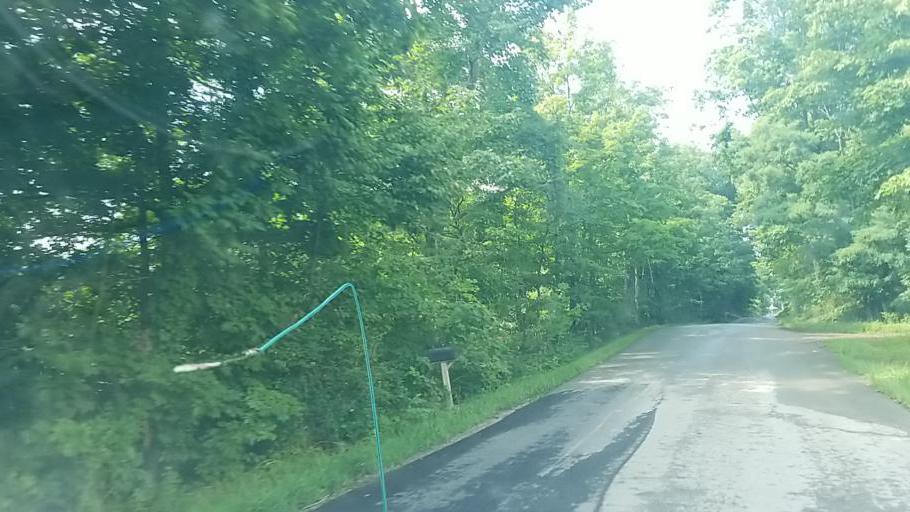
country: US
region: Ohio
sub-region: Medina County
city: Lodi
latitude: 41.0173
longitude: -81.9868
